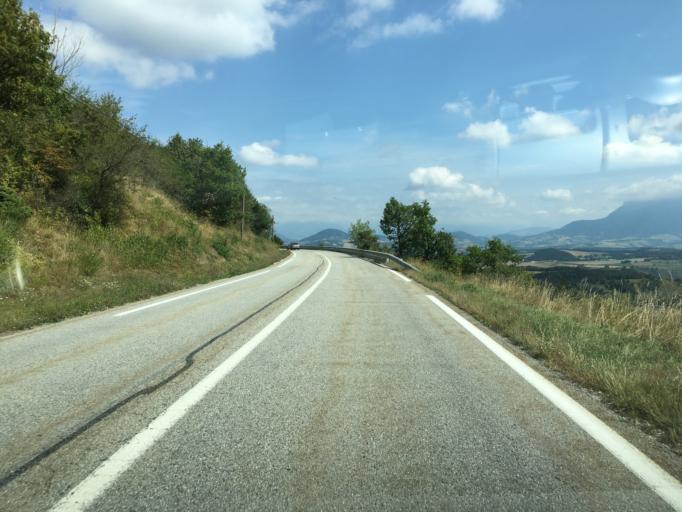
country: FR
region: Rhone-Alpes
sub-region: Departement de l'Isere
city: Mens
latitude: 44.7677
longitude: 5.6617
